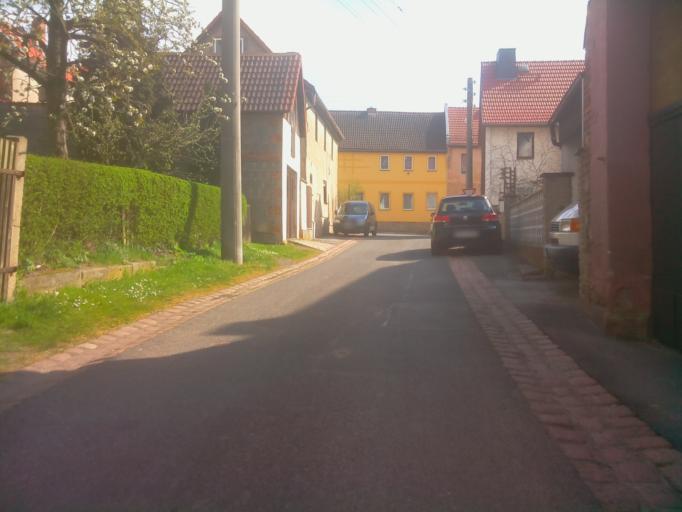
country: DE
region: Thuringia
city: Freienorla
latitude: 50.7705
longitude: 11.5432
